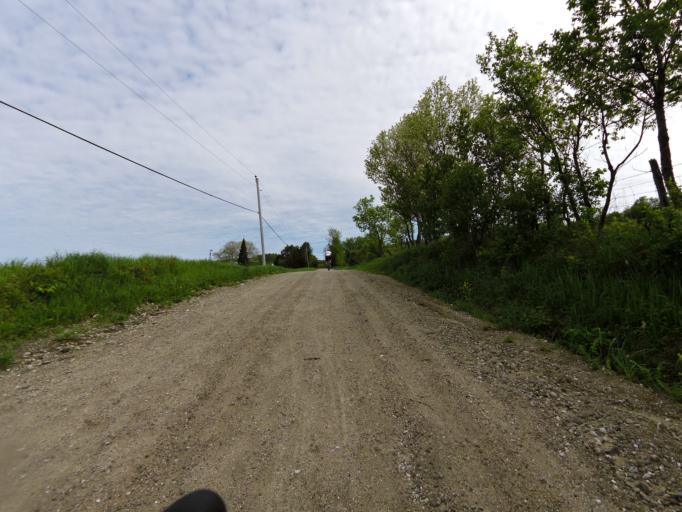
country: CA
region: Quebec
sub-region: Outaouais
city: Wakefield
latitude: 45.7386
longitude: -75.8898
